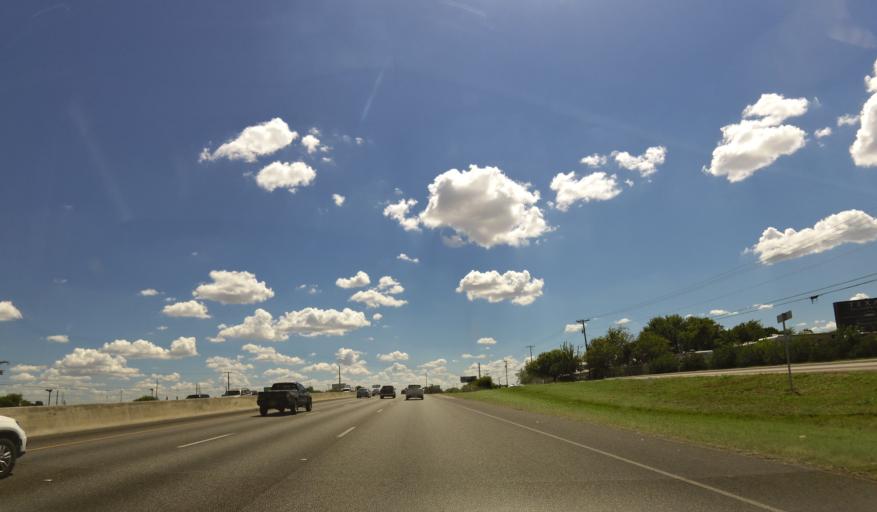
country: US
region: Texas
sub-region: Guadalupe County
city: Northcliff
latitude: 29.6488
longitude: -98.1970
